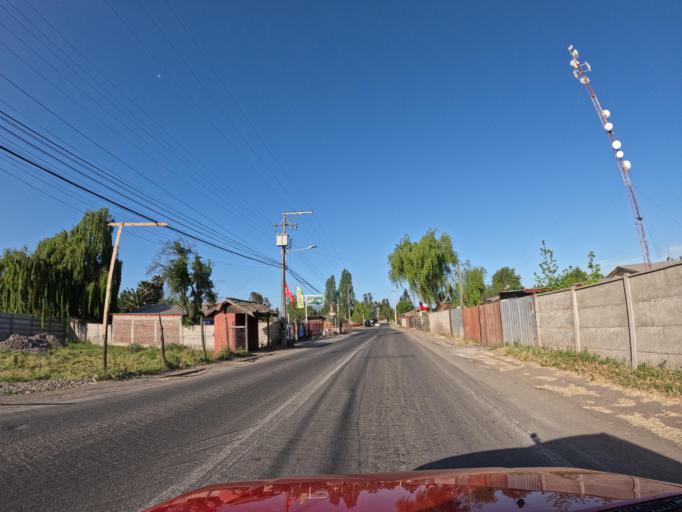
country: CL
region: O'Higgins
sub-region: Provincia de Colchagua
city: Santa Cruz
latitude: -34.6560
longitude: -71.3425
